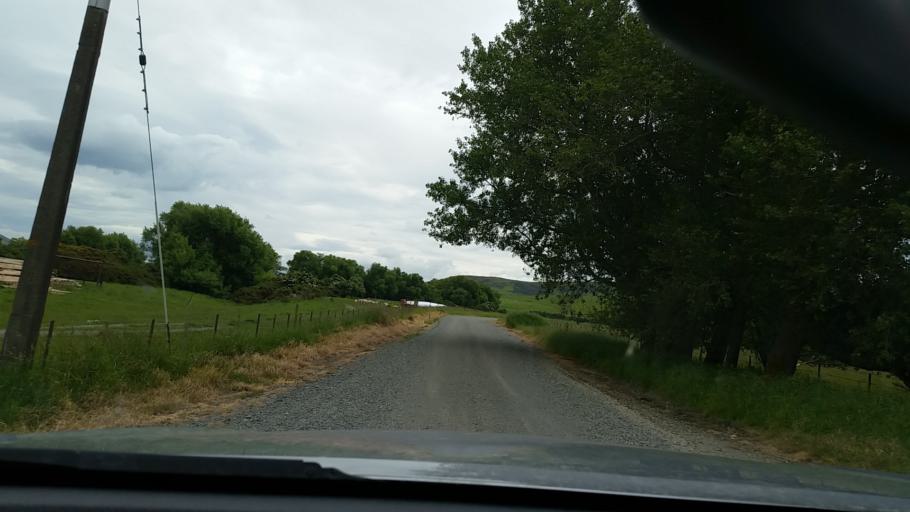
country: NZ
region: Southland
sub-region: Southland District
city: Winton
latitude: -45.8353
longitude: 168.1432
